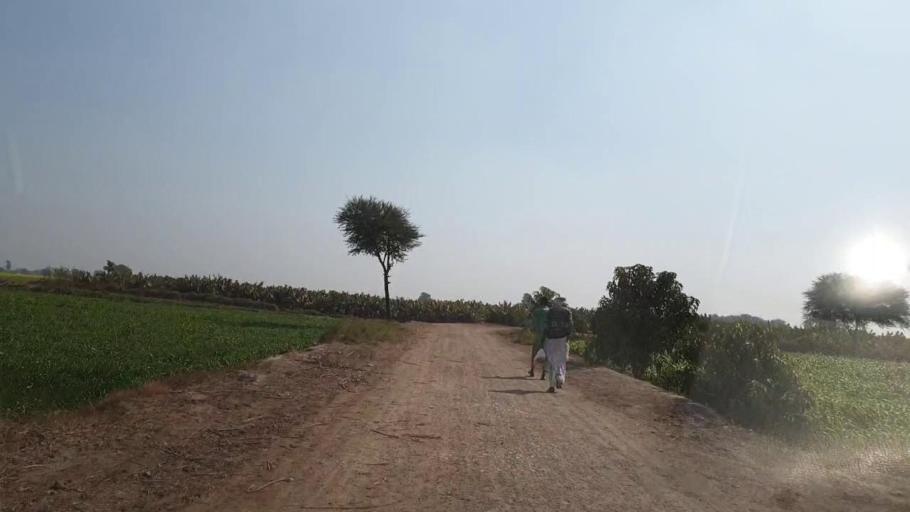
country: PK
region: Sindh
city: Tando Jam
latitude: 25.4974
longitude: 68.4796
